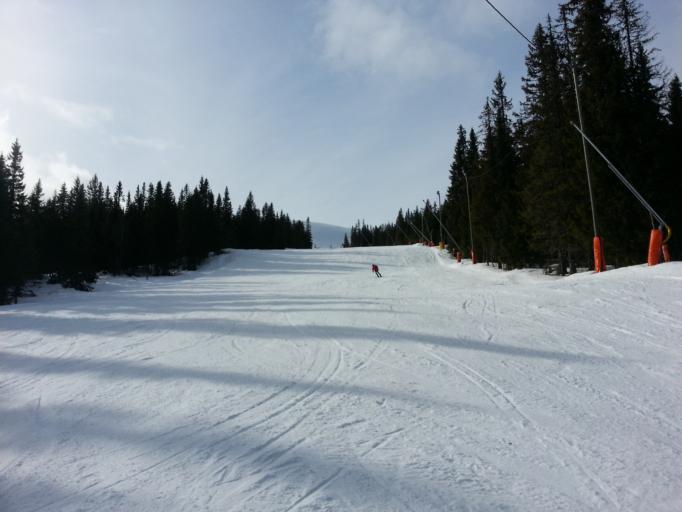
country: NO
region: Hedmark
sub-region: Trysil
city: Innbygda
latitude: 61.3115
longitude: 12.2164
